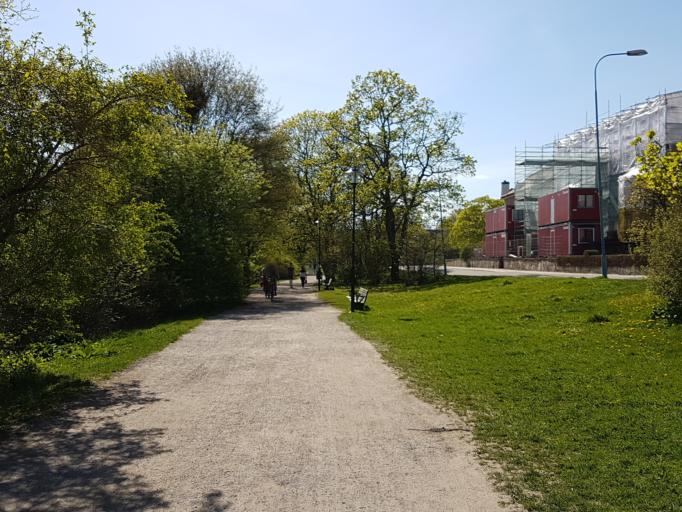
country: SE
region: Stockholm
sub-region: Stockholms Kommun
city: OEstermalm
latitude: 59.3325
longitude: 18.1055
